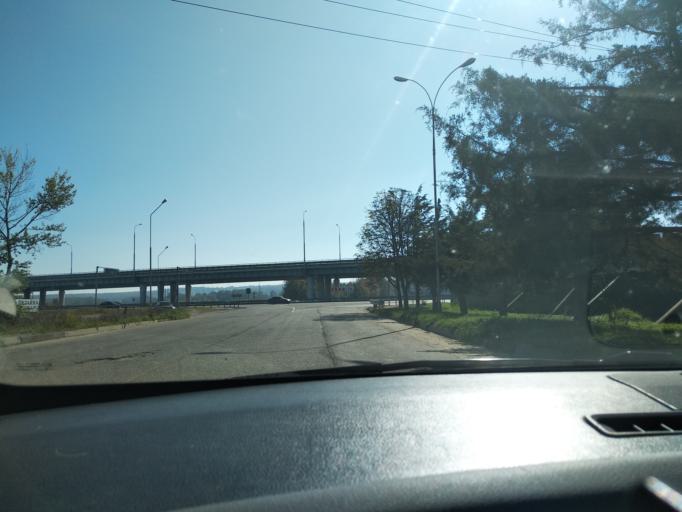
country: RU
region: Krasnodarskiy
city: Goryachiy Klyuch
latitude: 44.6458
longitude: 39.1291
